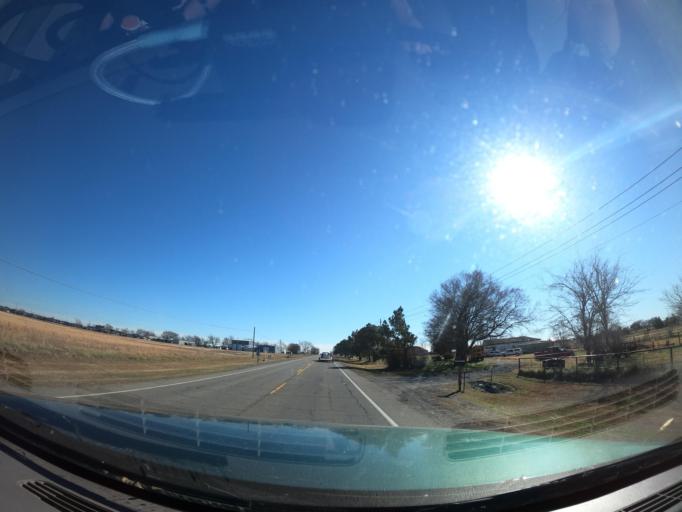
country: US
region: Oklahoma
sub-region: Muskogee County
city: Haskell
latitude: 35.8046
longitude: -95.6729
